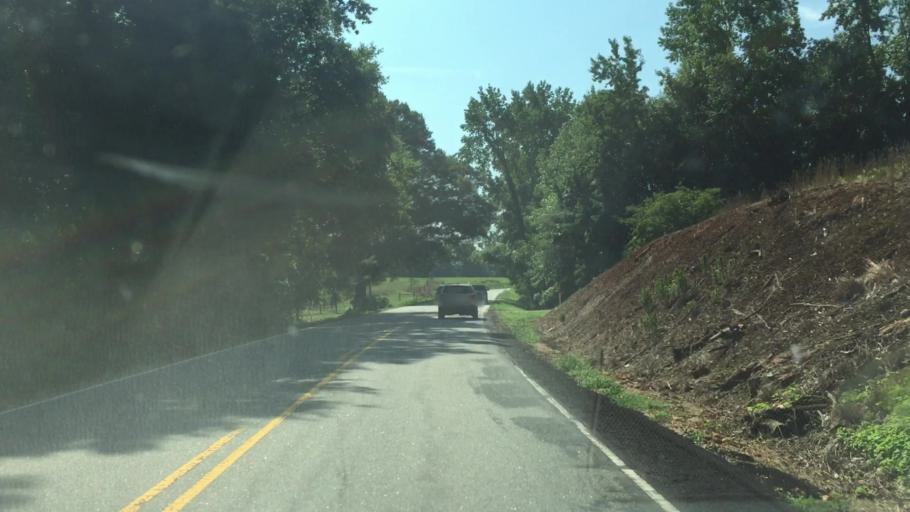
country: US
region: North Carolina
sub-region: Anson County
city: Burnsville
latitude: 35.0904
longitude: -80.2969
